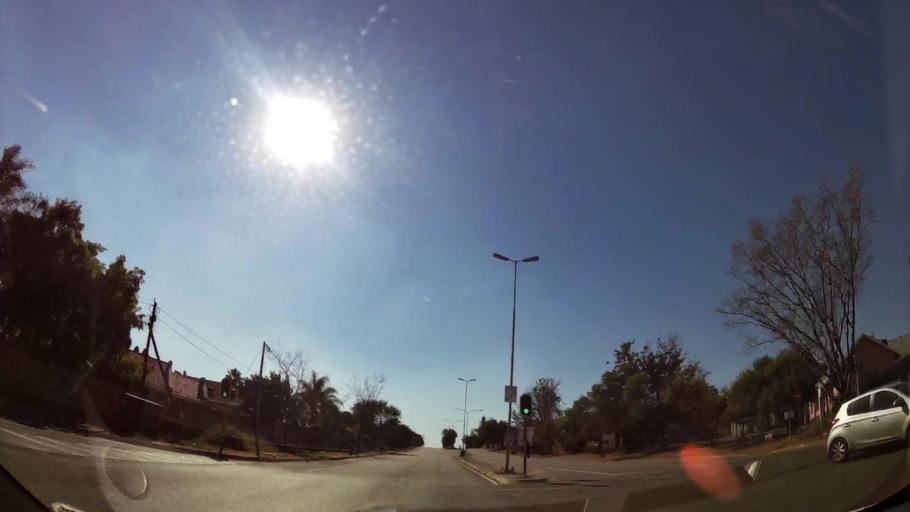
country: ZA
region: Gauteng
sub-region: City of Tshwane Metropolitan Municipality
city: Centurion
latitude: -25.8464
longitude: 28.2008
